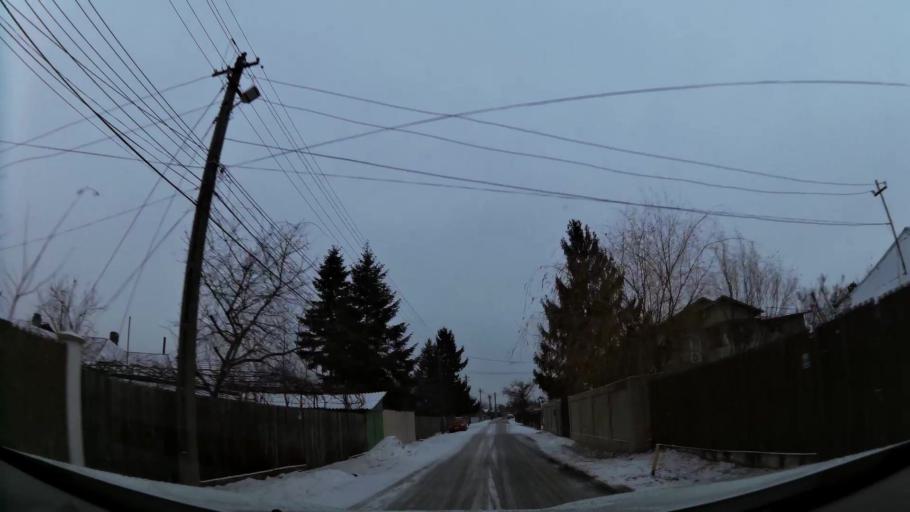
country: RO
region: Prahova
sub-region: Comuna Berceni
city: Corlatesti
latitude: 44.9126
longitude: 26.0918
